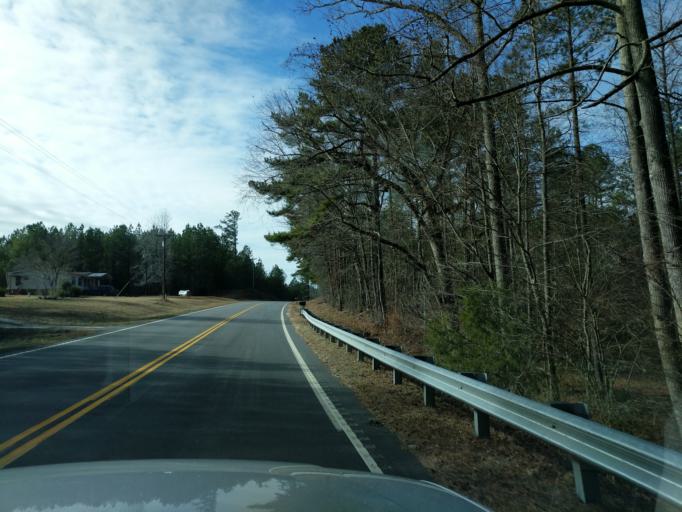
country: US
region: South Carolina
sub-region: Edgefield County
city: Edgefield
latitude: 33.9388
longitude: -81.9355
